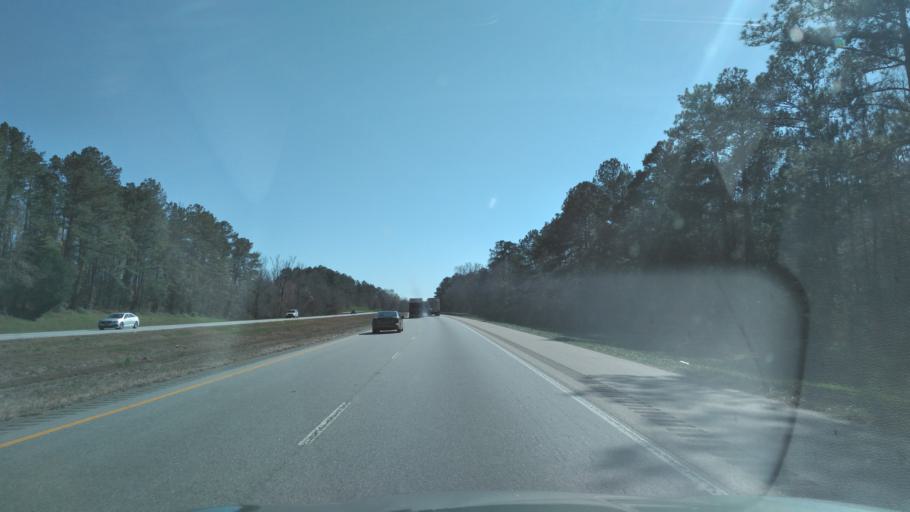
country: US
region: Alabama
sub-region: Lowndes County
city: Fort Deposit
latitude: 32.0399
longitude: -86.5069
